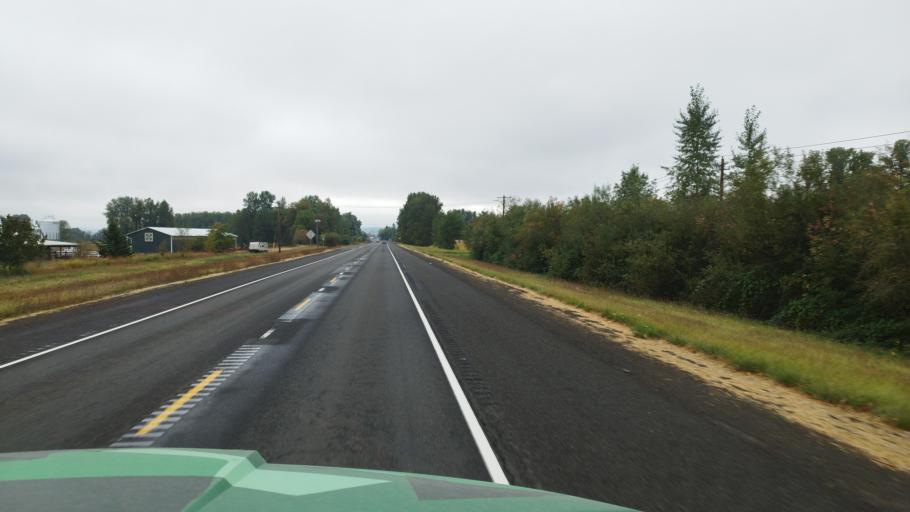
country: US
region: Oregon
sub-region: Washington County
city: Forest Grove
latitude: 45.4480
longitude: -123.1425
